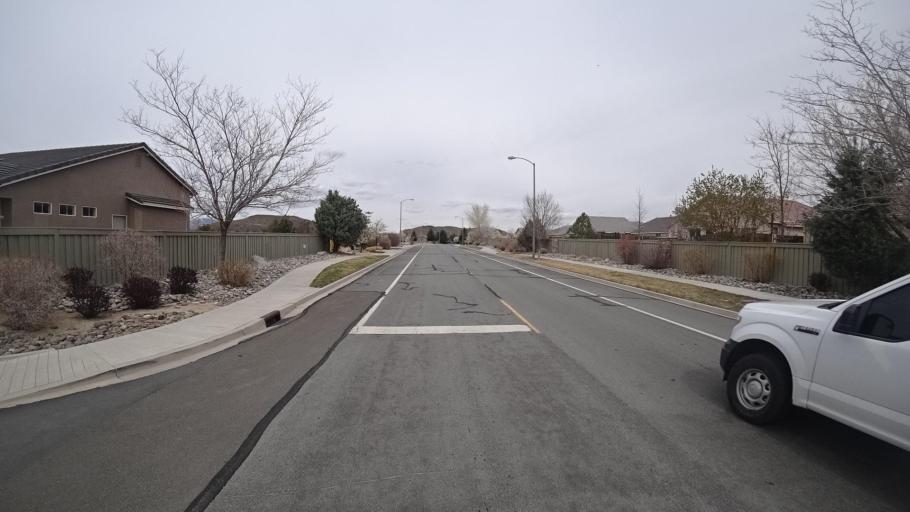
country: US
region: Nevada
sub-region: Washoe County
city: Sparks
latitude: 39.4430
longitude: -119.7362
